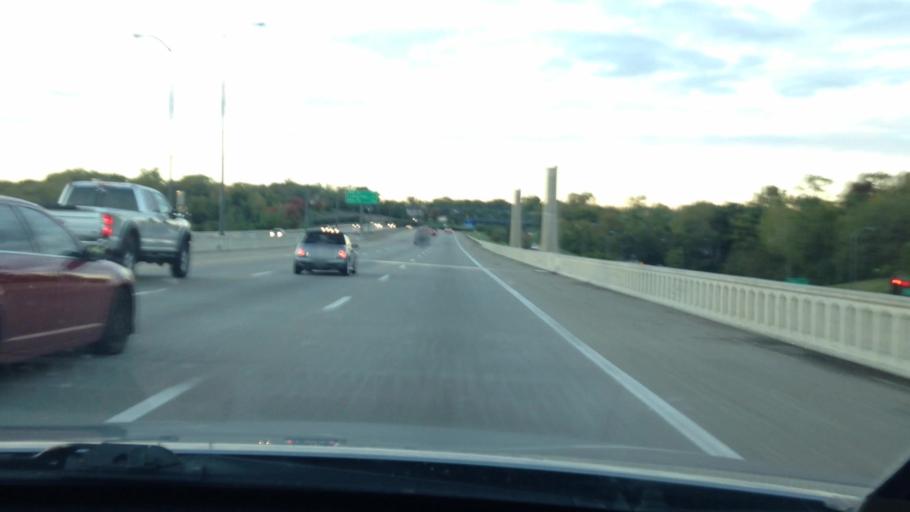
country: US
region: Kansas
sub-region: Johnson County
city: Westwood
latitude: 39.0421
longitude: -94.5594
